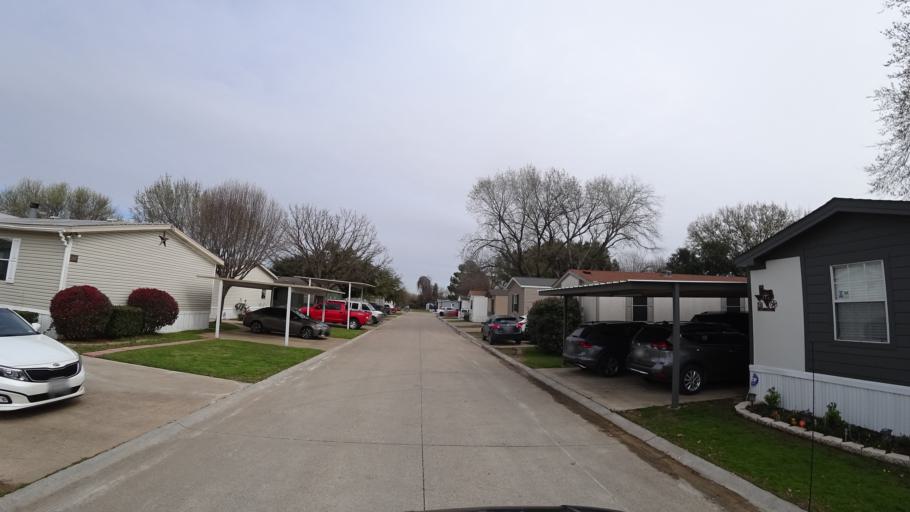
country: US
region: Texas
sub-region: Denton County
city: Lewisville
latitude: 33.0328
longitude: -96.9846
